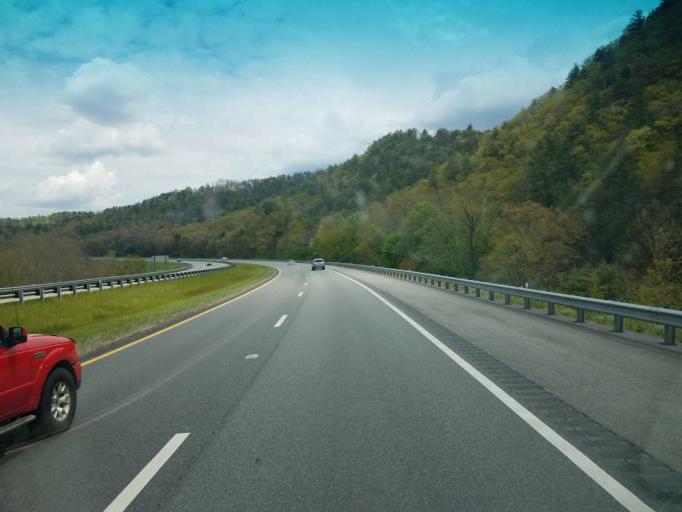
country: US
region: Virginia
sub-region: Bland County
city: Bland
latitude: 37.1933
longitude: -81.1162
